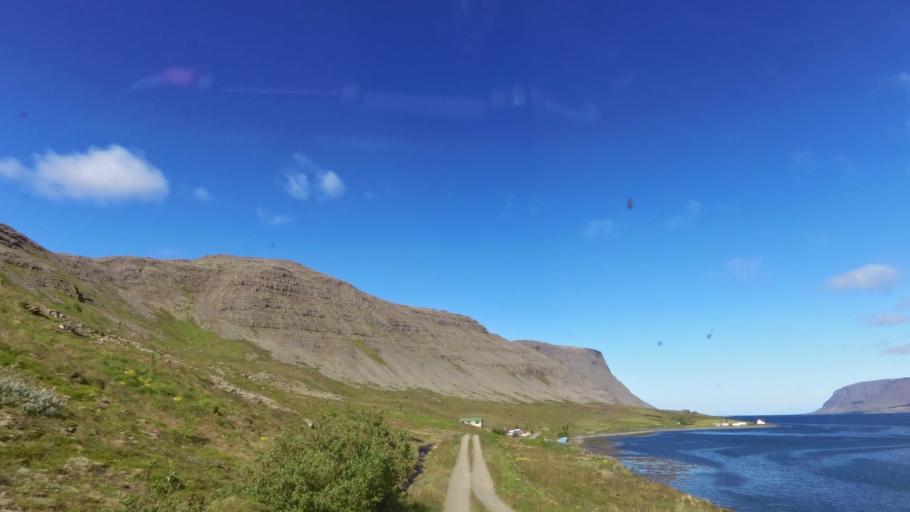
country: IS
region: West
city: Olafsvik
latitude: 65.6172
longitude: -23.8553
